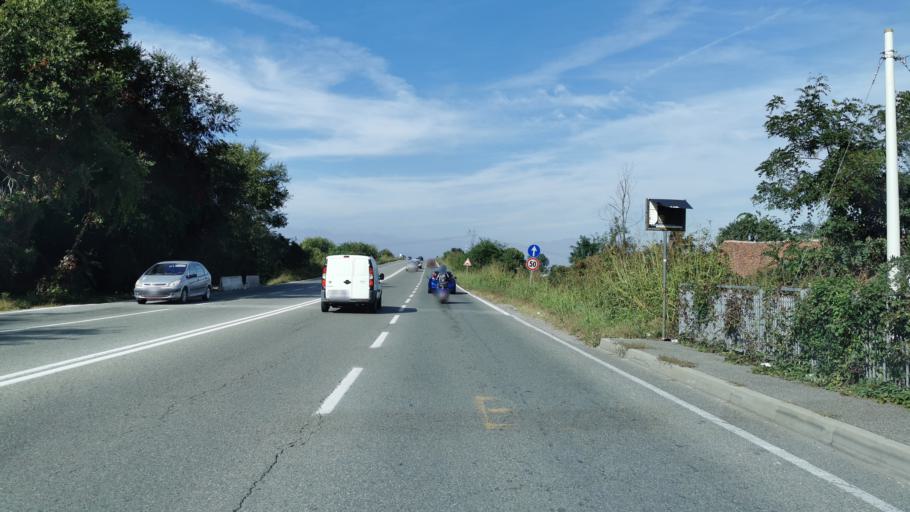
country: IT
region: Piedmont
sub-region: Provincia di Torino
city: Borgaro Torinese
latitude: 45.1233
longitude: 7.6606
